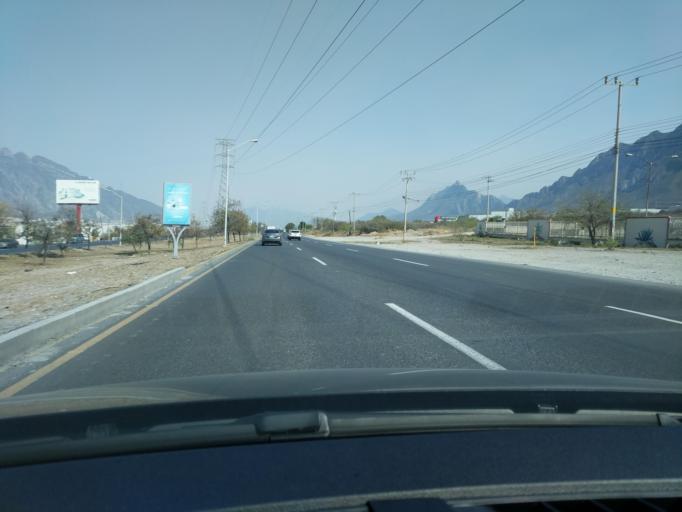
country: MX
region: Nuevo Leon
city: Santa Catarina
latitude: 25.6925
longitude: -100.5104
